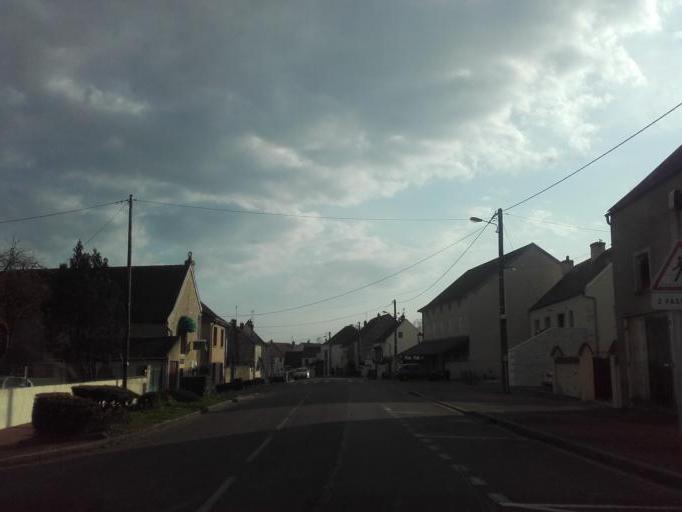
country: FR
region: Bourgogne
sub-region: Departement de la Cote-d'Or
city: Corpeau
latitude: 46.9296
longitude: 4.7525
